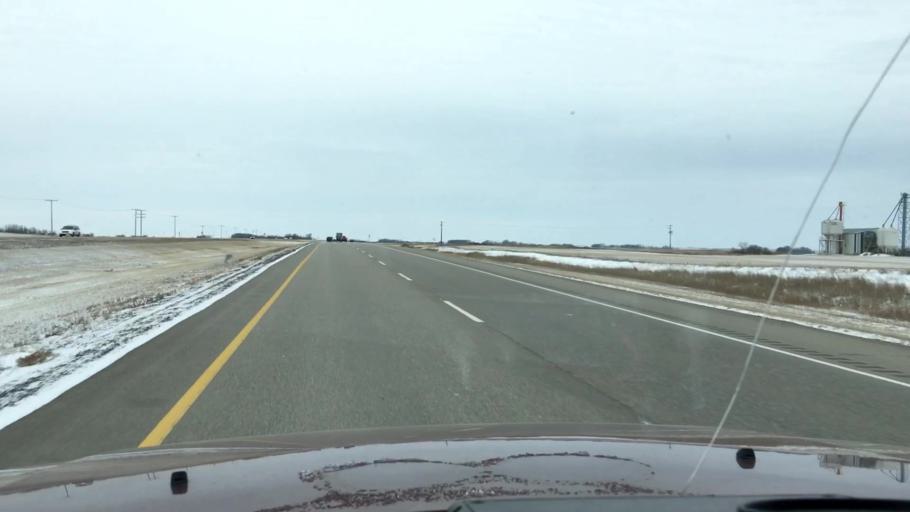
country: CA
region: Saskatchewan
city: Watrous
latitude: 51.2155
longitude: -105.9617
